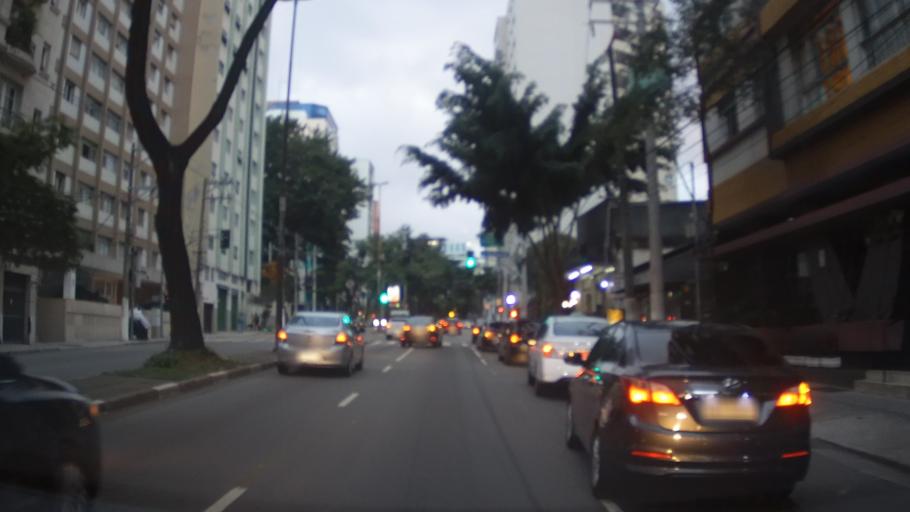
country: BR
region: Sao Paulo
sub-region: Sao Paulo
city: Sao Paulo
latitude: -23.5656
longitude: -46.6450
